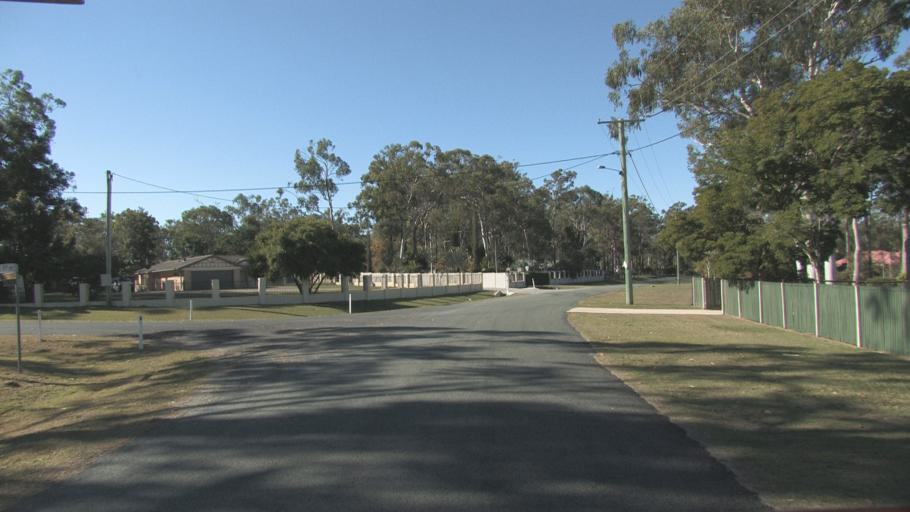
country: AU
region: Queensland
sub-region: Logan
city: Chambers Flat
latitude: -27.7353
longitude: 153.0677
